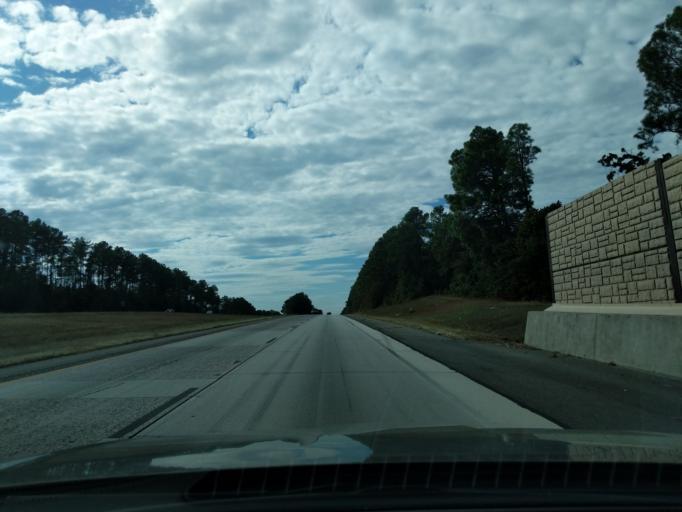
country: US
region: Georgia
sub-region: Columbia County
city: Grovetown
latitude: 33.4802
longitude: -82.1615
